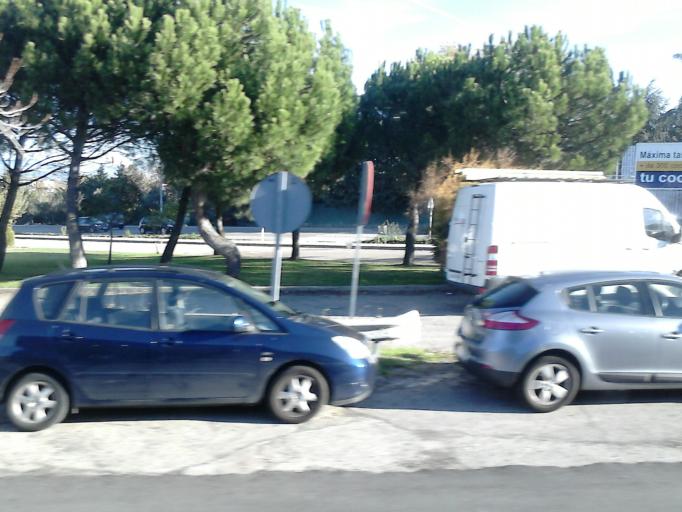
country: ES
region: Madrid
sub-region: Provincia de Madrid
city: Las Rozas de Madrid
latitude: 40.4867
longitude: -3.8674
